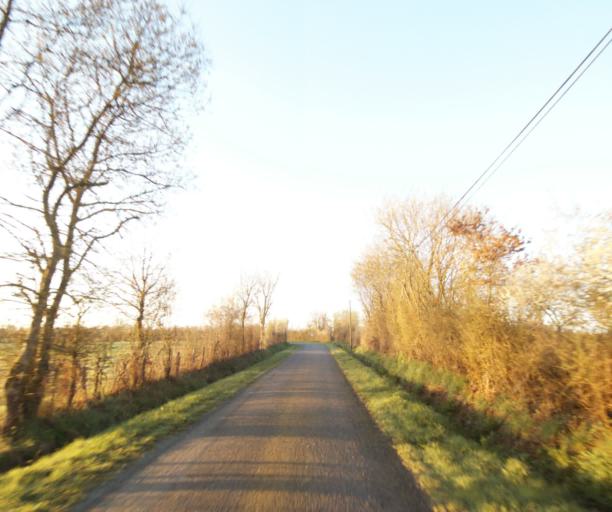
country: FR
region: Pays de la Loire
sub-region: Departement de la Loire-Atlantique
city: Bouvron
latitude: 47.4227
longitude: -1.8816
